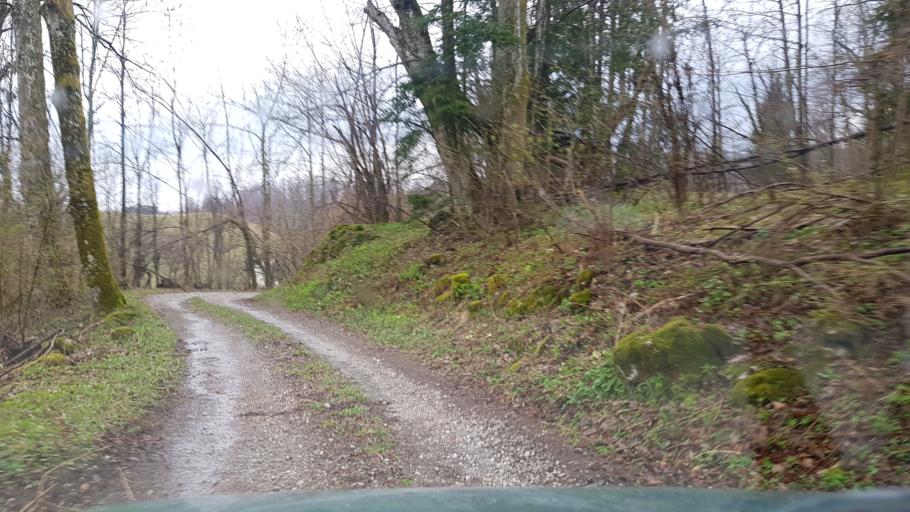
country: SI
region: Cerkno
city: Cerkno
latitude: 46.1341
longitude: 13.8593
